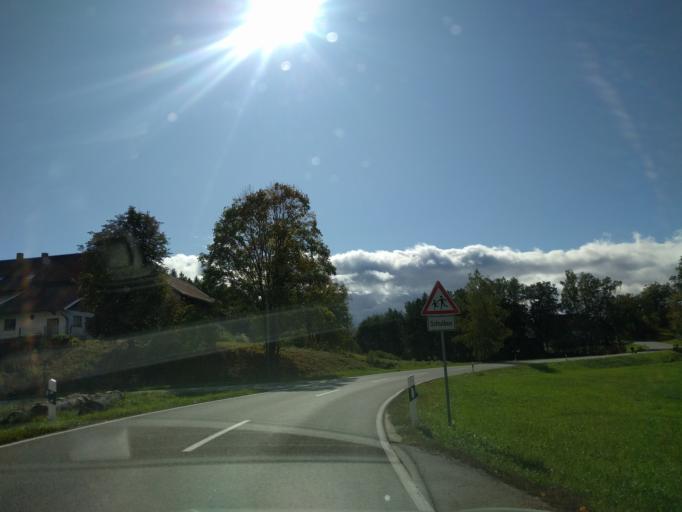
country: DE
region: Bavaria
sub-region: Lower Bavaria
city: Hengersberg
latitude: 48.7992
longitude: 13.0508
